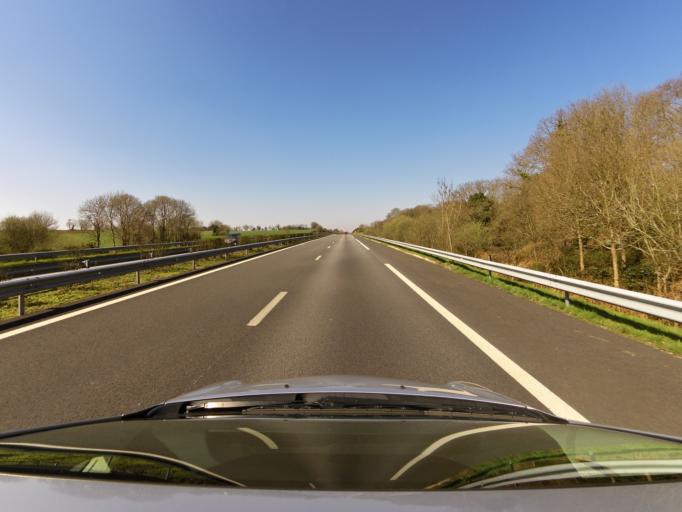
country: FR
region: Brittany
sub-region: Departement du Morbihan
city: Augan
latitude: 47.9250
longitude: -2.2210
